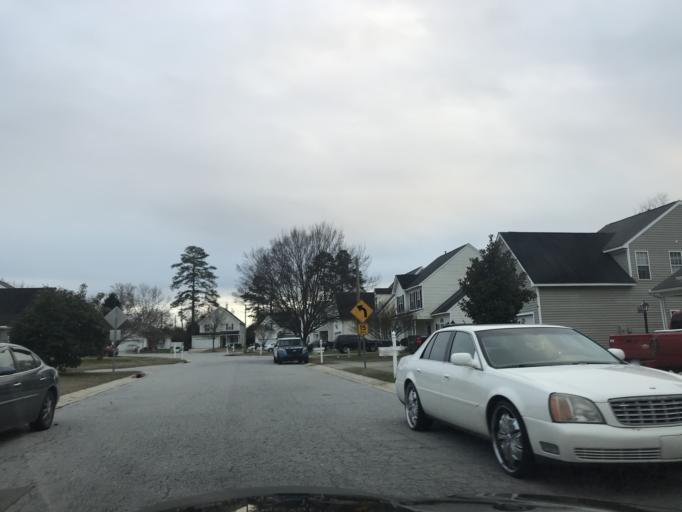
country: US
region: North Carolina
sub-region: Wake County
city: Garner
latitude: 35.7488
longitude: -78.6026
